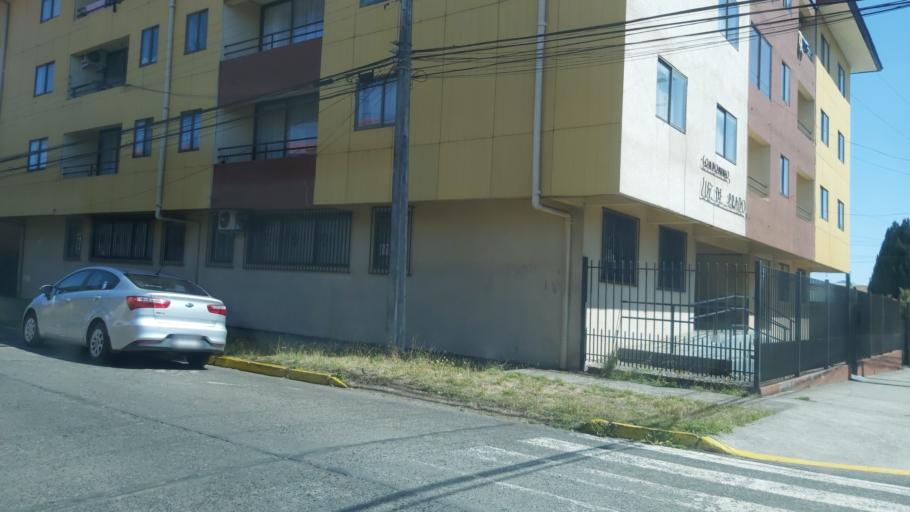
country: CL
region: Araucania
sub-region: Provincia de Malleco
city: Victoria
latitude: -38.2314
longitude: -72.3309
